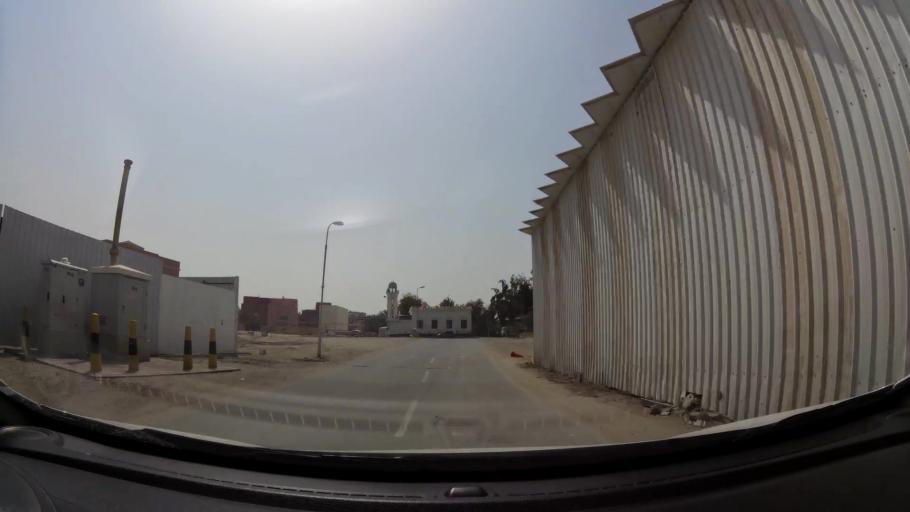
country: BH
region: Manama
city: Jidd Hafs
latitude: 26.2317
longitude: 50.5014
